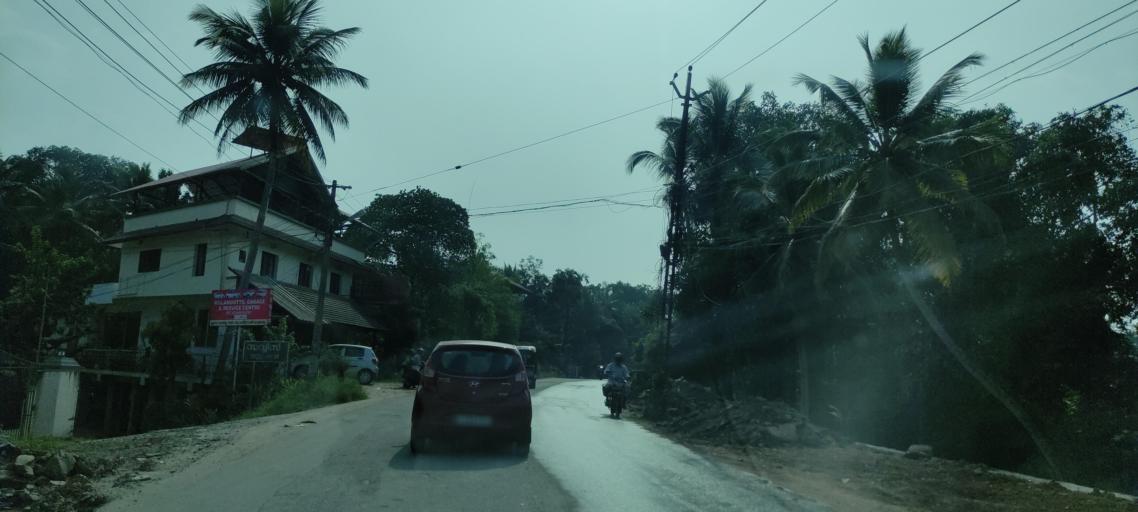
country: IN
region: Kerala
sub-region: Pattanamtitta
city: Tiruvalla
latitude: 9.3786
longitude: 76.5599
